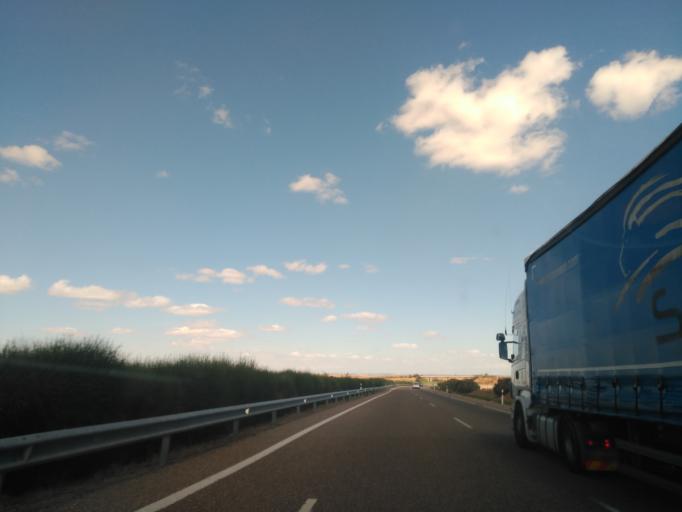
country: ES
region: Castille and Leon
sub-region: Provincia de Zamora
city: Castrillo de la Guarena
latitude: 41.2486
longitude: -5.2928
